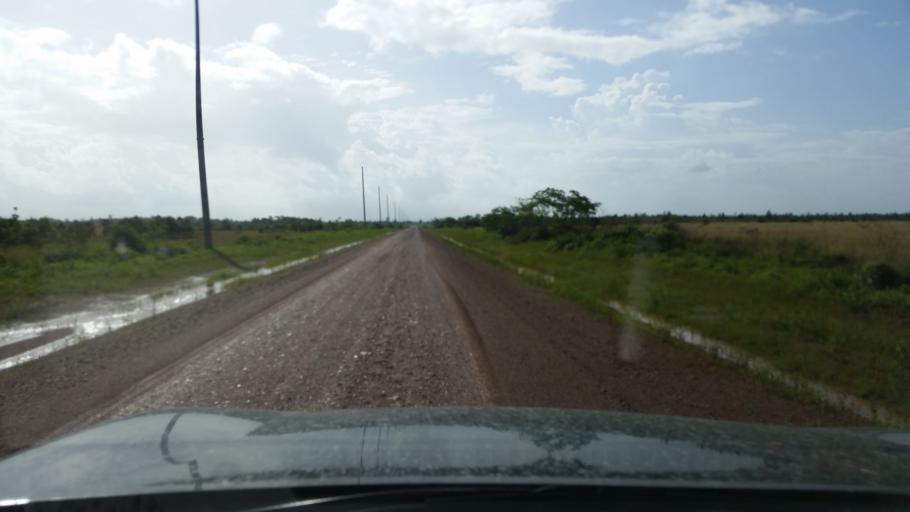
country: NI
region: Atlantico Norte (RAAN)
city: Puerto Cabezas
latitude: 14.1093
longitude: -83.5879
